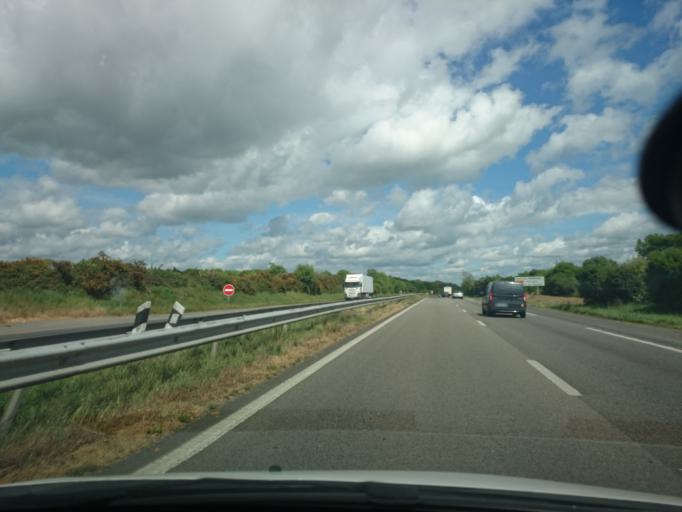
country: FR
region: Pays de la Loire
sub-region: Departement de la Loire-Atlantique
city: Prinquiau
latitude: 47.3563
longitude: -2.0519
